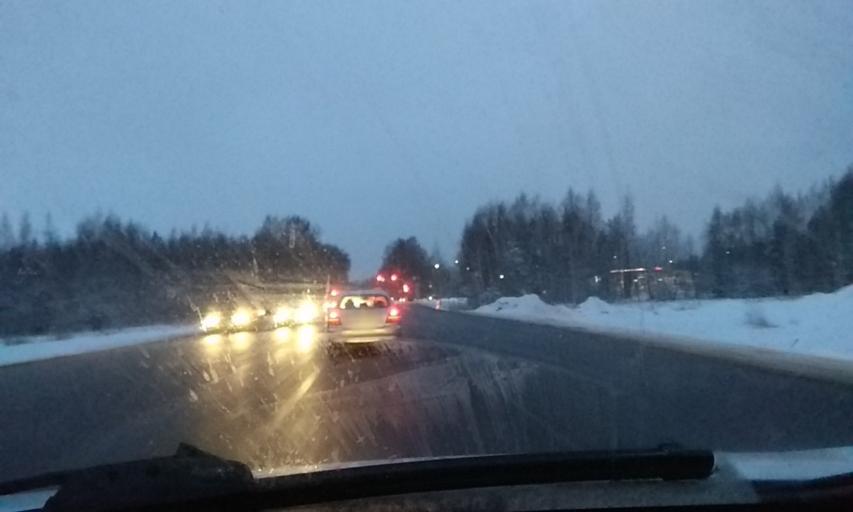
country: LT
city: Ramuciai
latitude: 54.9189
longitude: 24.0424
